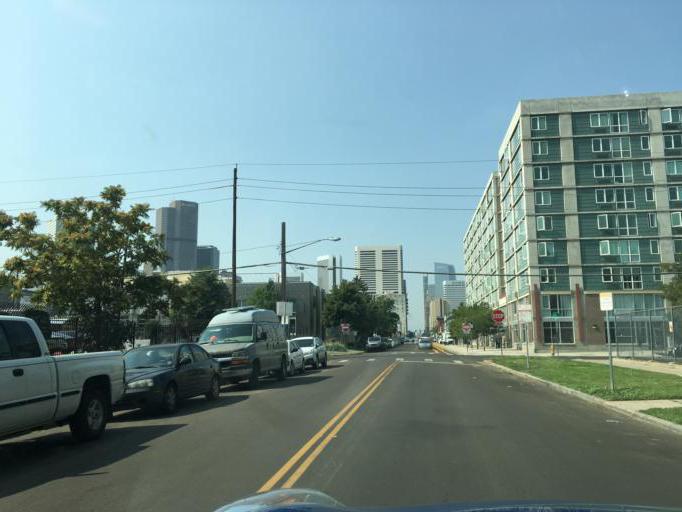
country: US
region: Colorado
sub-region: Denver County
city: Denver
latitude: 39.7557
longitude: -104.9855
